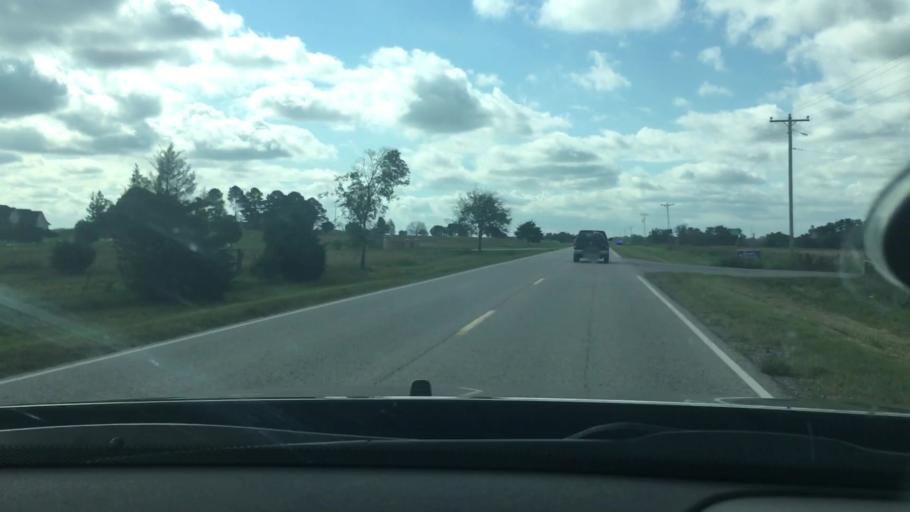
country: US
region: Oklahoma
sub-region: Pontotoc County
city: Ada
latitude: 34.7168
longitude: -96.6349
